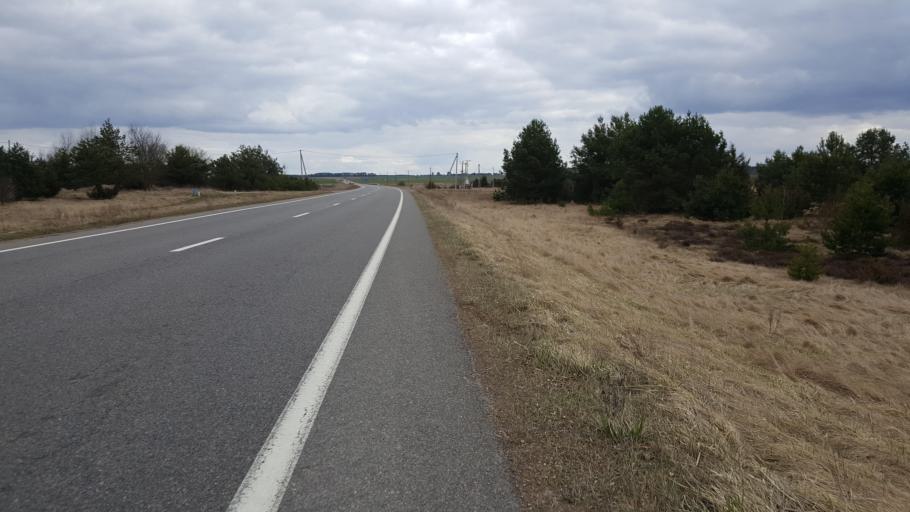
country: BY
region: Brest
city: Kamyanyets
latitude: 52.4245
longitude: 23.8391
